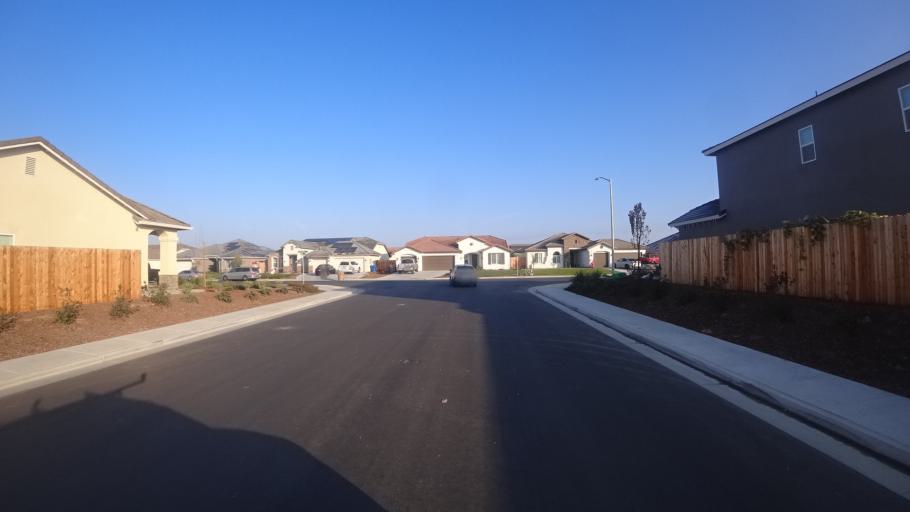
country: US
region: California
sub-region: Kern County
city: Greenacres
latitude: 35.2892
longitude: -119.1124
